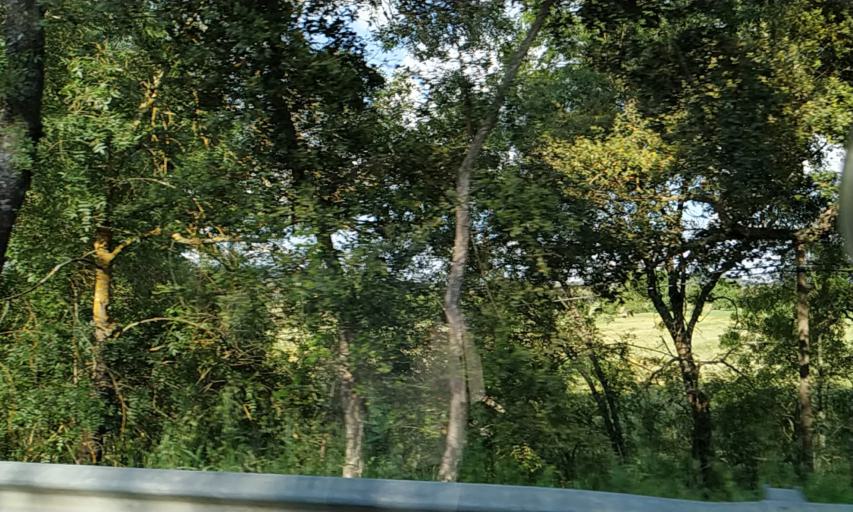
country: PT
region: Portalegre
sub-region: Portalegre
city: Urra
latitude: 39.1985
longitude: -7.4579
